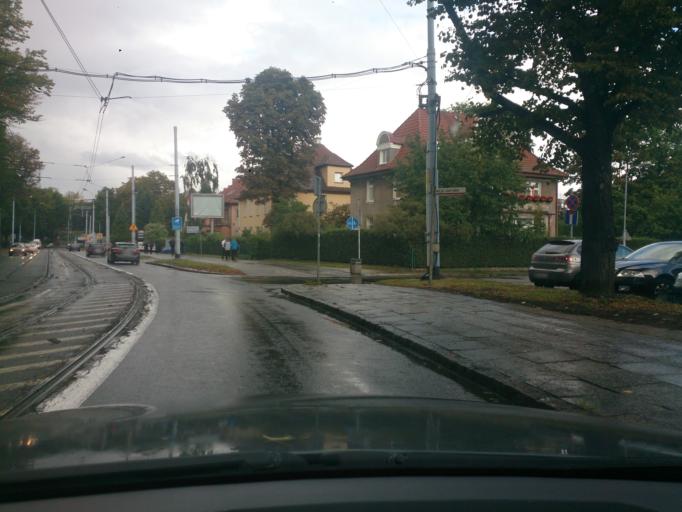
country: PL
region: Pomeranian Voivodeship
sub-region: Gdansk
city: Gdansk
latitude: 54.3736
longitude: 18.6252
